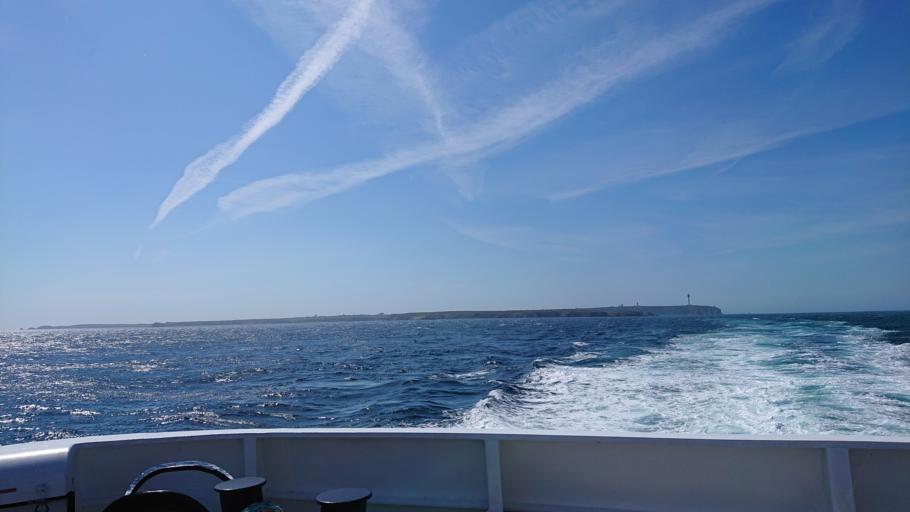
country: FR
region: Brittany
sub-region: Departement du Finistere
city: Porspoder
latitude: 48.4531
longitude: -5.0104
